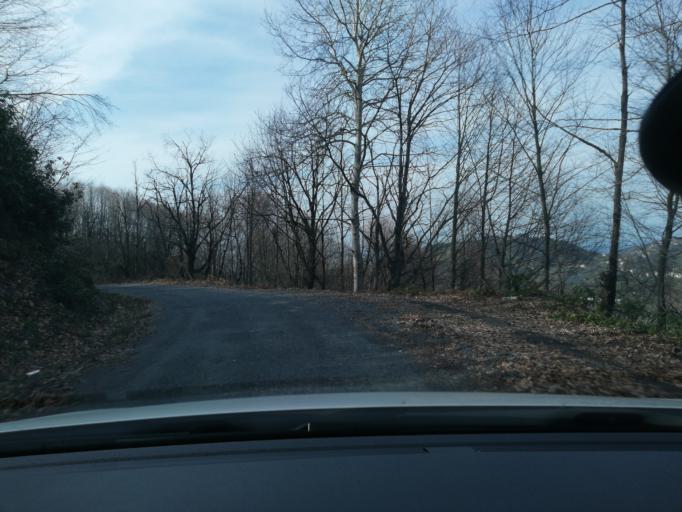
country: TR
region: Zonguldak
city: Kozlu
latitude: 41.3521
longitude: 31.6320
